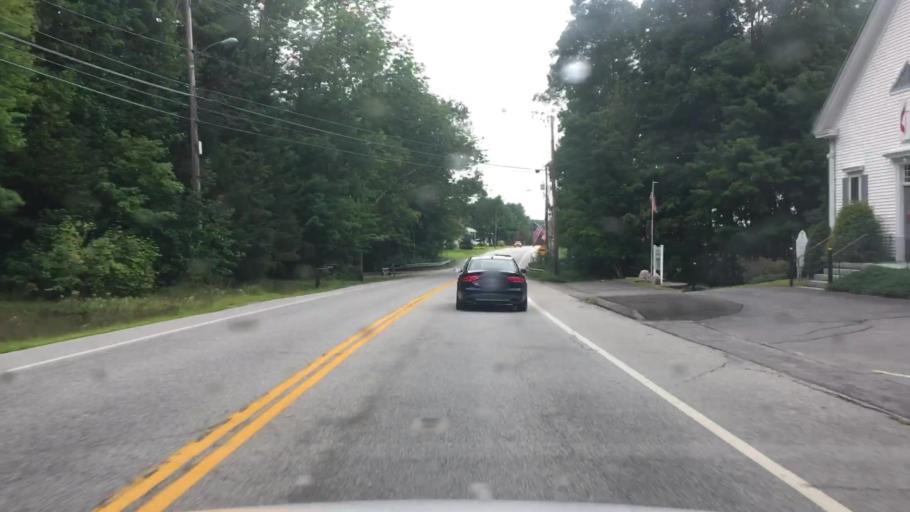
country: US
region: Maine
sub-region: York County
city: Cornish
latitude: 43.8353
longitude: -70.7787
